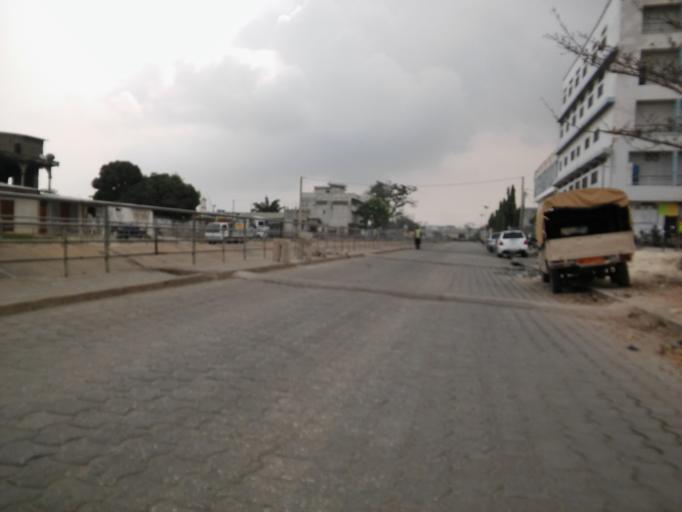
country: BJ
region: Littoral
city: Cotonou
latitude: 6.3879
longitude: 2.4213
